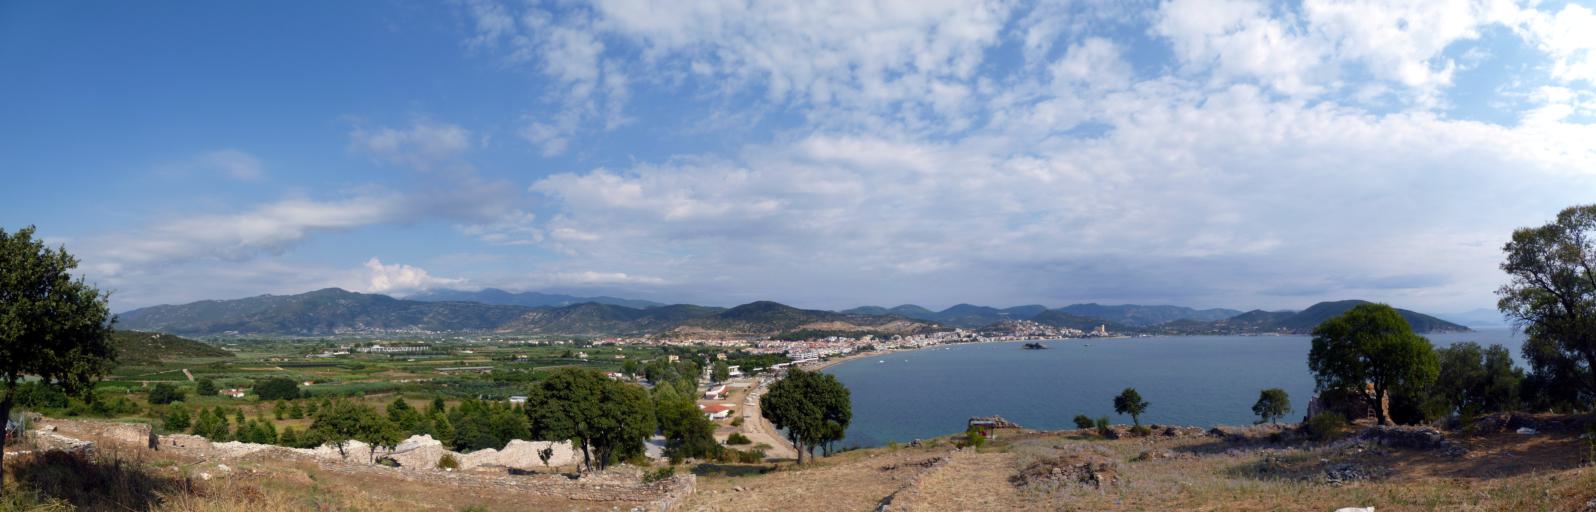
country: GR
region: East Macedonia and Thrace
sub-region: Nomos Kavalas
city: Nea Peramos
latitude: 40.8247
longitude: 24.3089
